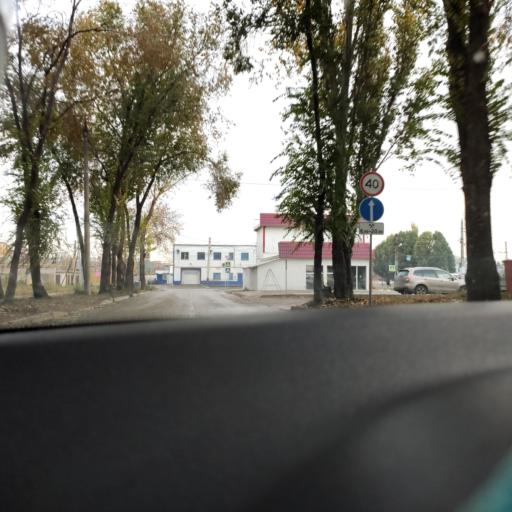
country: RU
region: Samara
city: Samara
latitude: 53.1984
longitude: 50.2460
